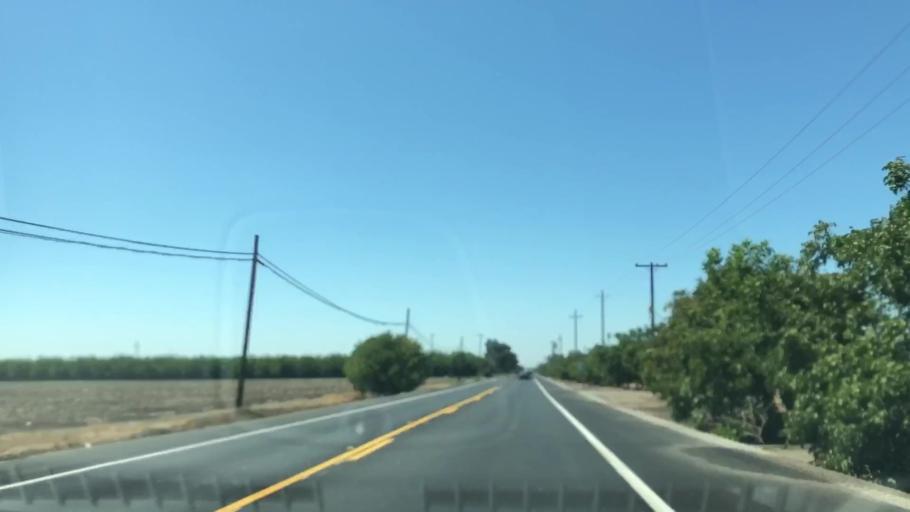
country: US
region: California
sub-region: San Joaquin County
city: Garden Acres
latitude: 37.9516
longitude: -121.1927
